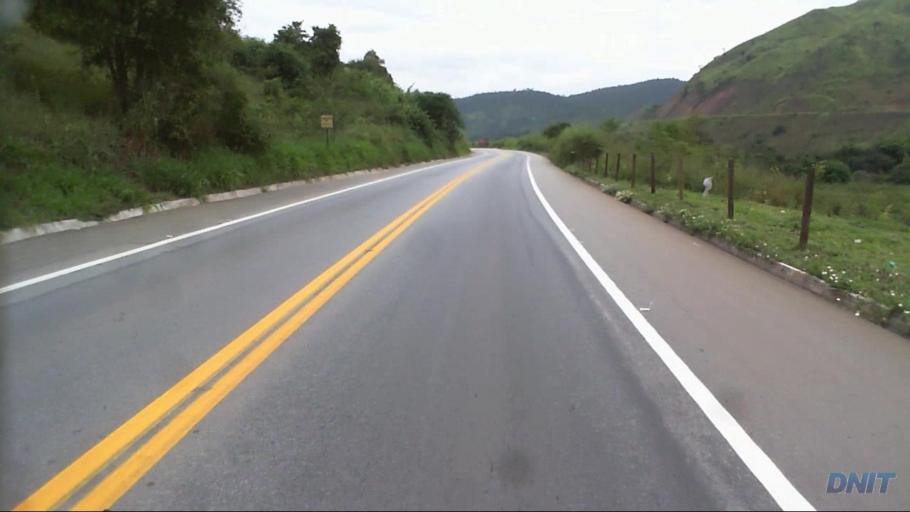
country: BR
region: Minas Gerais
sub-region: Timoteo
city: Timoteo
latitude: -19.5987
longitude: -42.7495
